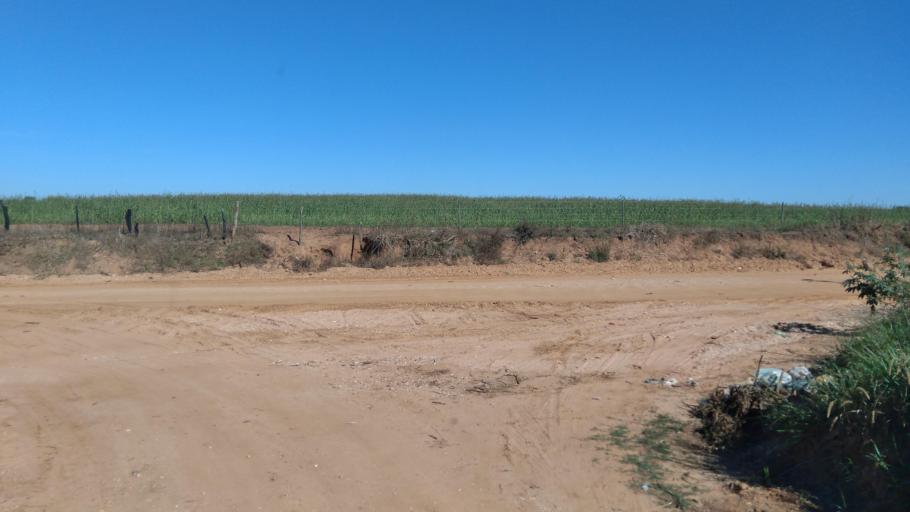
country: BR
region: Goias
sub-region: Mineiros
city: Mineiros
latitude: -17.5951
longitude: -52.5561
